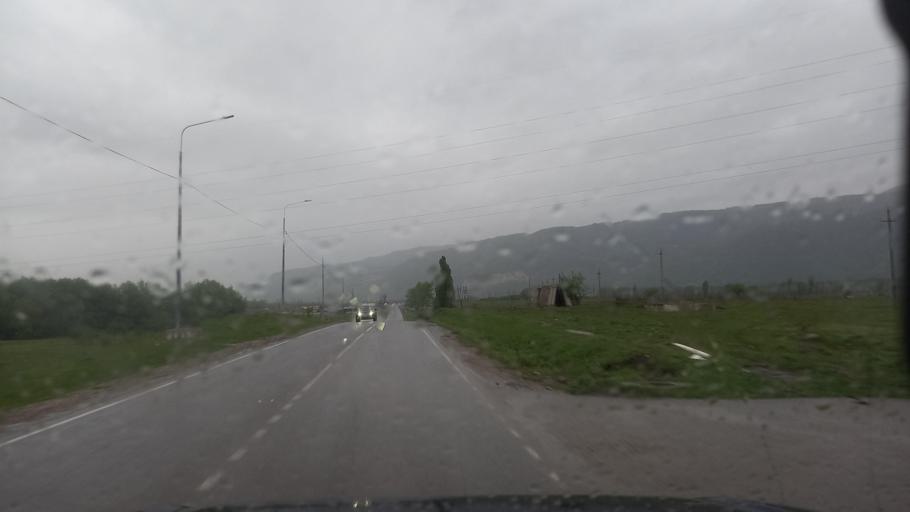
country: RU
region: Kabardino-Balkariya
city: Zhankhoteko
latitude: 43.5883
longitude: 43.2181
